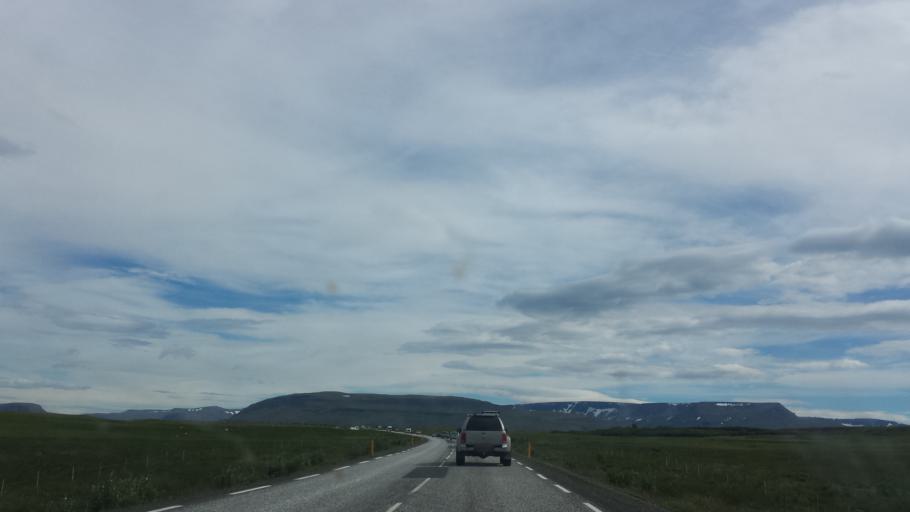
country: IS
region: West
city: Borgarnes
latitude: 64.3688
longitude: -21.8310
